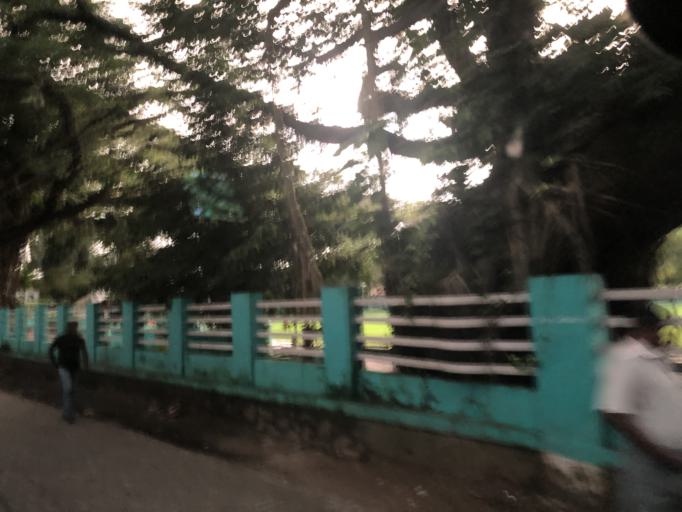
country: IN
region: Kerala
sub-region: Ernakulam
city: Cochin
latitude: 9.9524
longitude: 76.2450
